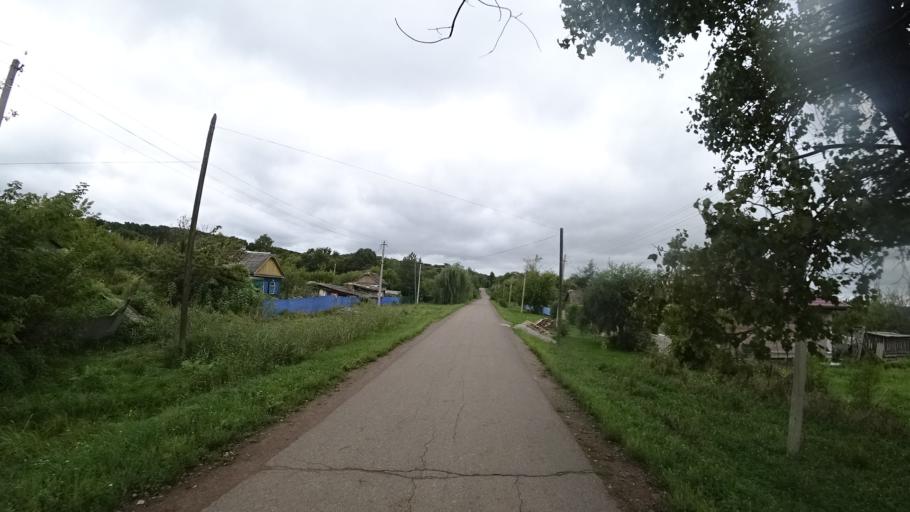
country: RU
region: Primorskiy
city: Chernigovka
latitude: 44.4562
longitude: 132.5904
